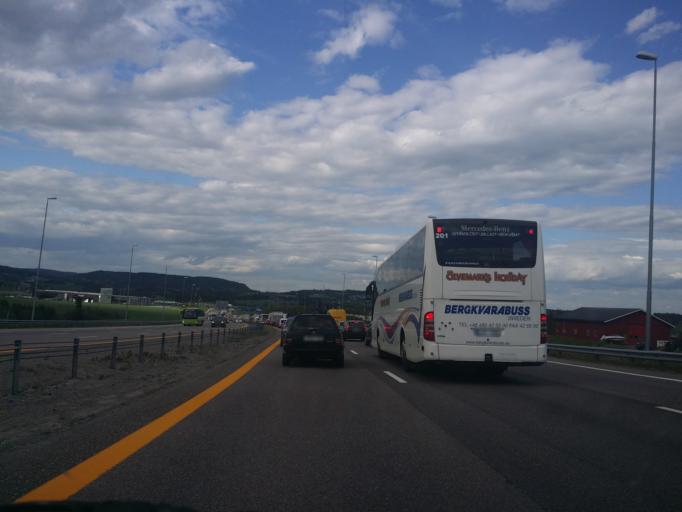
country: NO
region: Akershus
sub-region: Lorenskog
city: Kjenn
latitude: 59.9680
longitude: 10.9880
